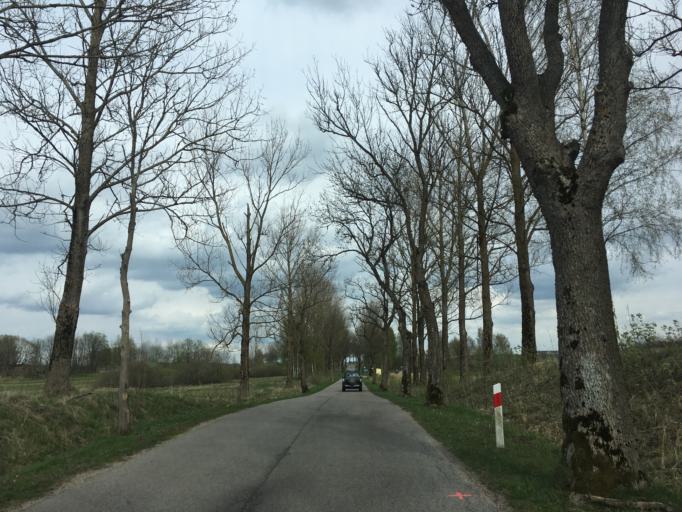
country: PL
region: Podlasie
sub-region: Powiat suwalski
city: Filipow
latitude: 54.3545
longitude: 22.7536
